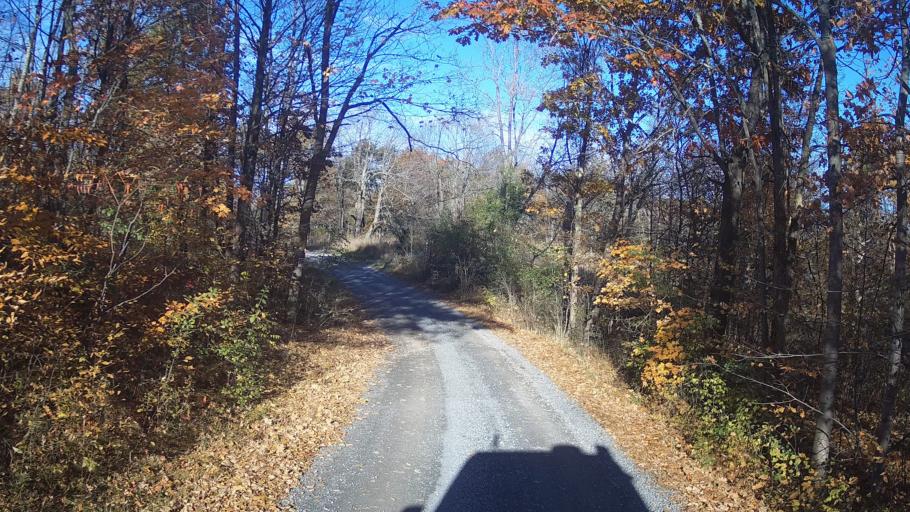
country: CA
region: Ontario
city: Perth
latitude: 44.7304
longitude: -76.4370
